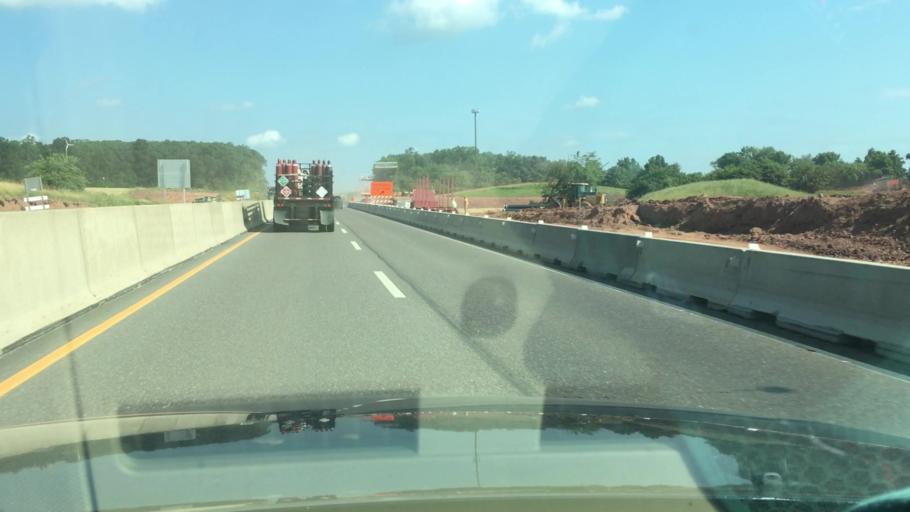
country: US
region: Pennsylvania
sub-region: Montgomery County
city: Harleysville
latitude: 40.2760
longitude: -75.3590
